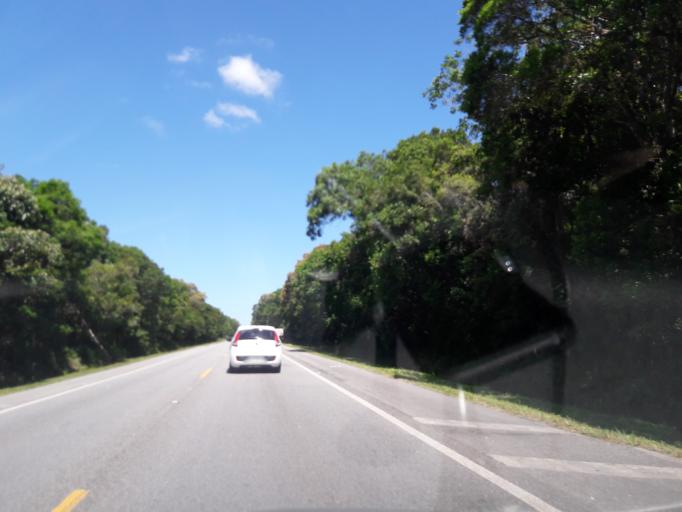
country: BR
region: Parana
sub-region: Pontal Do Parana
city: Pontal do Parana
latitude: -25.6045
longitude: -48.5556
